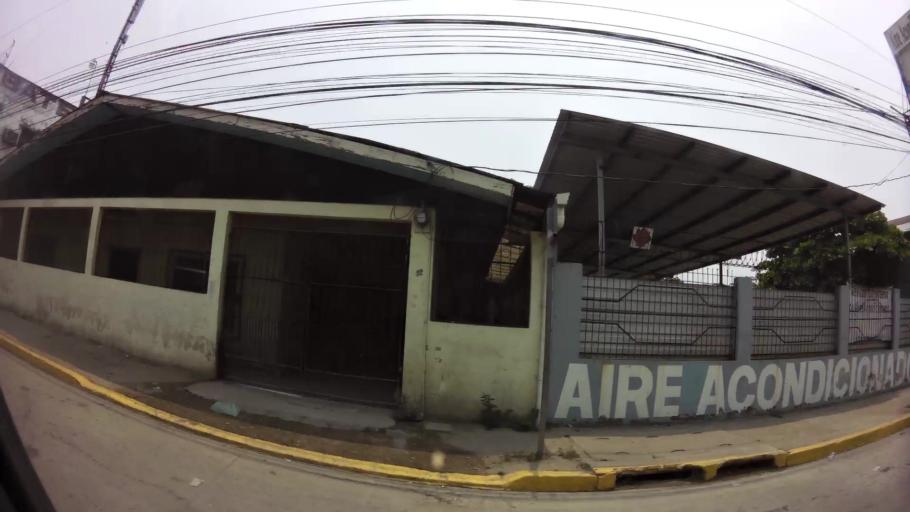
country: HN
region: Yoro
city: El Progreso
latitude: 15.4023
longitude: -87.8142
